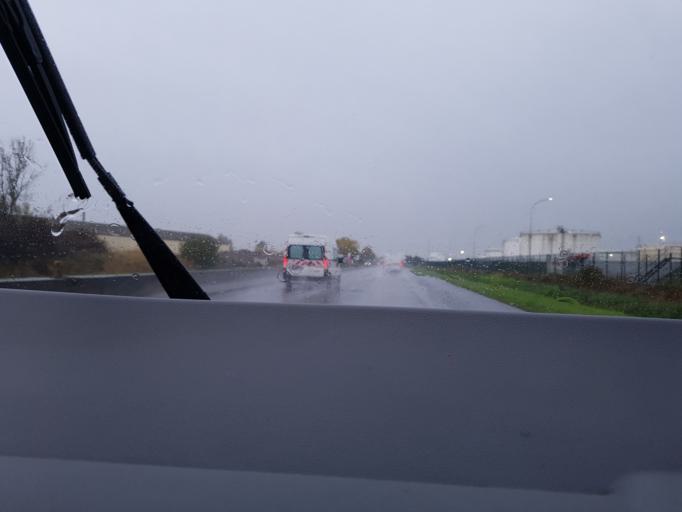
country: FR
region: Aquitaine
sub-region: Departement de la Gironde
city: Saint-Louis-de-Montferrand
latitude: 44.9203
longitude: -0.5416
